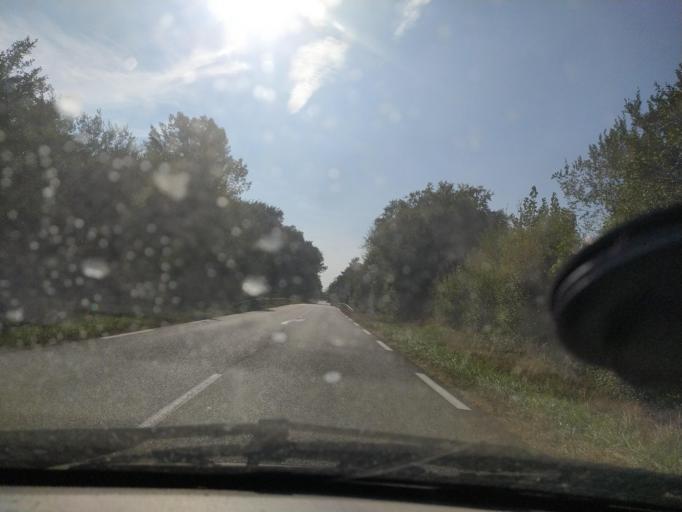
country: FR
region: Midi-Pyrenees
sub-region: Departement du Gers
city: Nogaro
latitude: 43.7831
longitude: -0.0224
